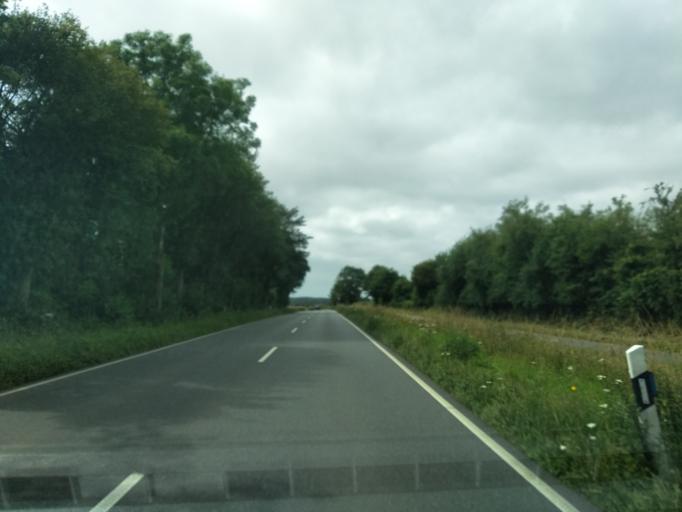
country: DE
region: Schleswig-Holstein
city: Munkbrarup
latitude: 54.8071
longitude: 9.5734
